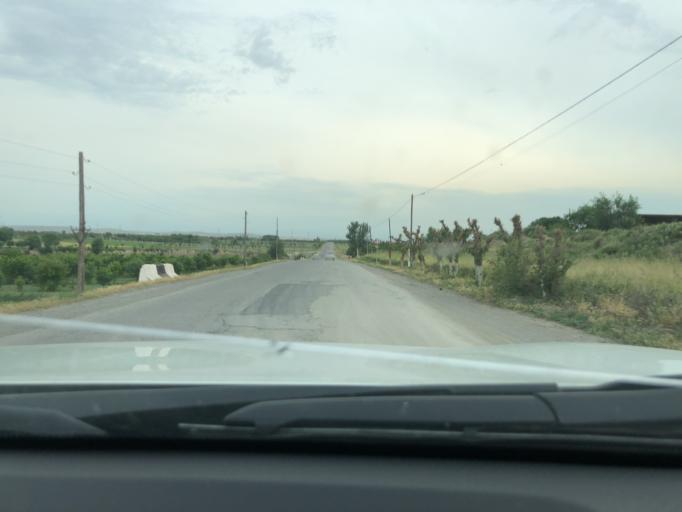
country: UZ
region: Toshkent
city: Bekobod
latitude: 40.1634
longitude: 69.2538
